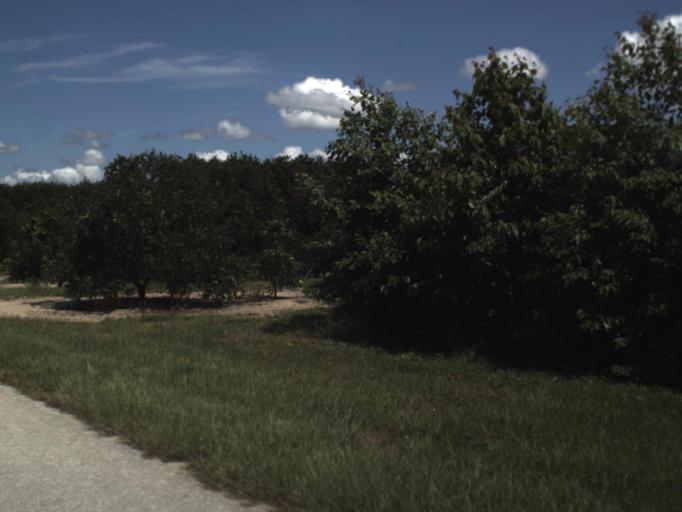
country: US
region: Florida
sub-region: Polk County
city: Lake Wales
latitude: 27.8774
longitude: -81.5814
